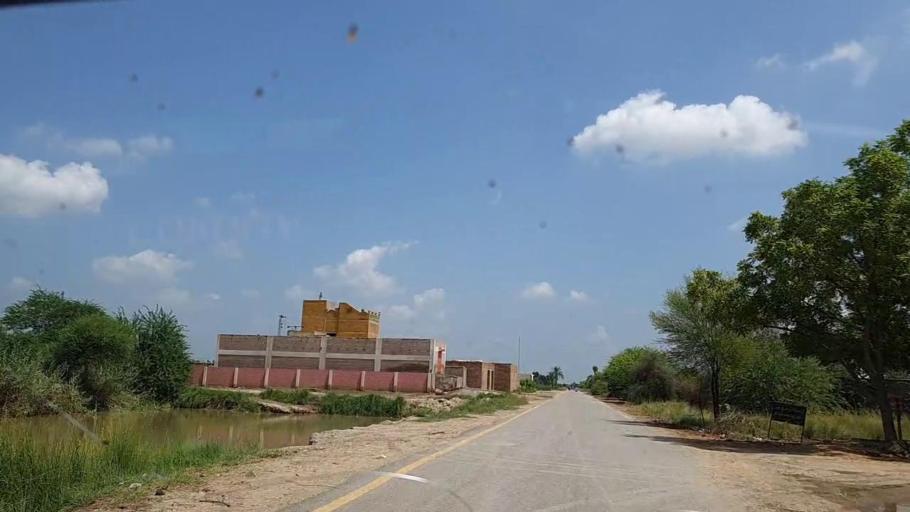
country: PK
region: Sindh
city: Tharu Shah
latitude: 26.9780
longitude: 68.0850
